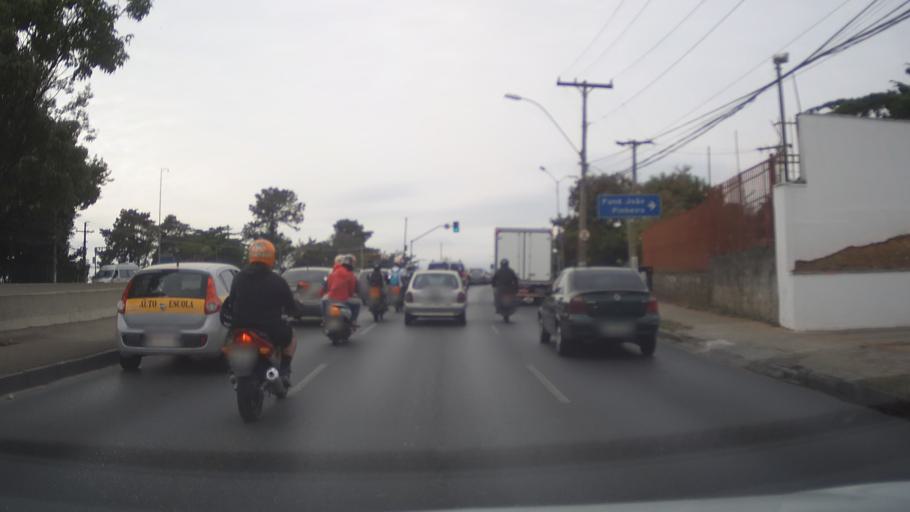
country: BR
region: Minas Gerais
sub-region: Belo Horizonte
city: Belo Horizonte
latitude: -19.8519
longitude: -43.9629
